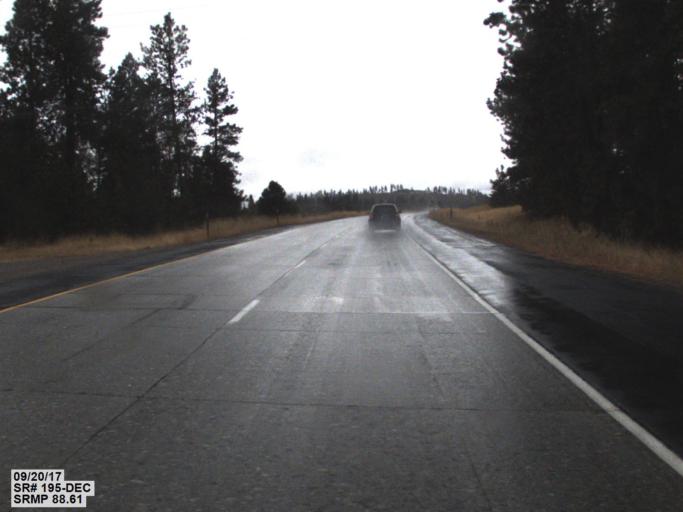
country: US
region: Washington
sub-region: Spokane County
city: Spokane
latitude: 47.5518
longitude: -117.3961
